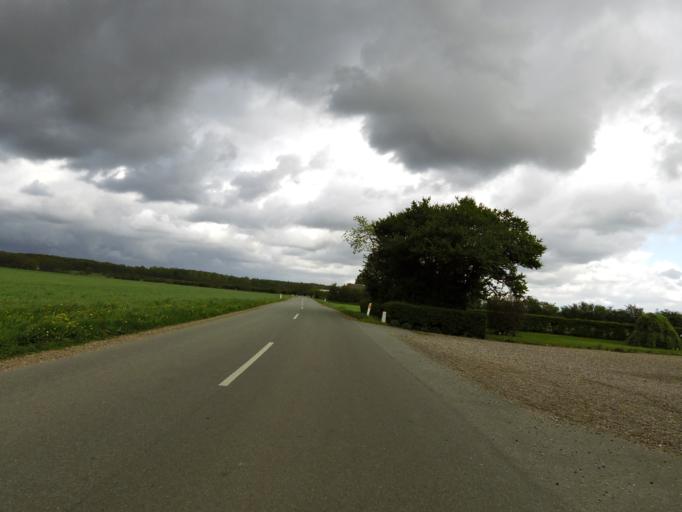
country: DK
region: South Denmark
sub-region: Haderslev Kommune
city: Gram
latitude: 55.3018
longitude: 9.0280
